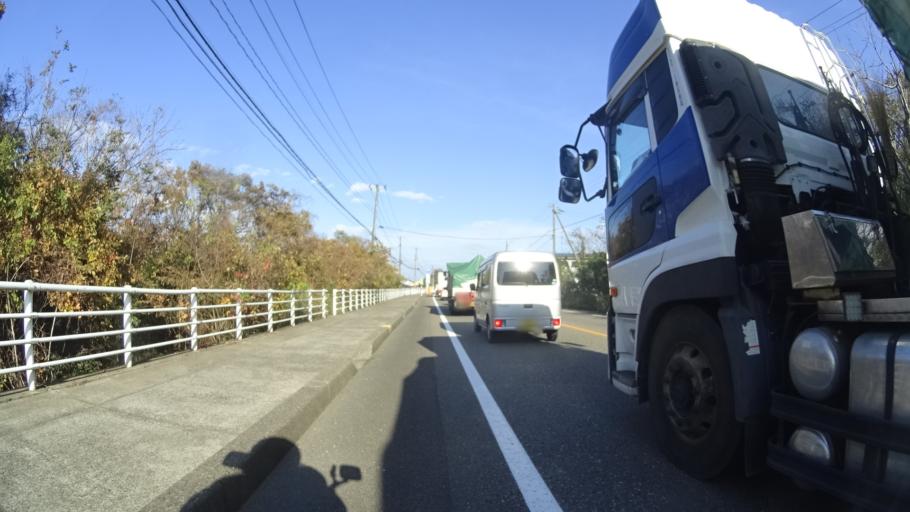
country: JP
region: Niigata
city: Joetsu
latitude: 37.2018
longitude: 138.2946
